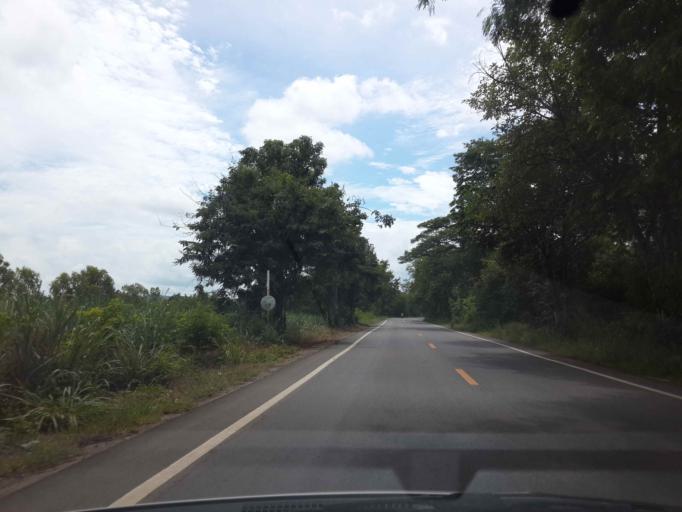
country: TH
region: Ratchaburi
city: Pak Tho
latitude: 13.4119
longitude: 99.6709
